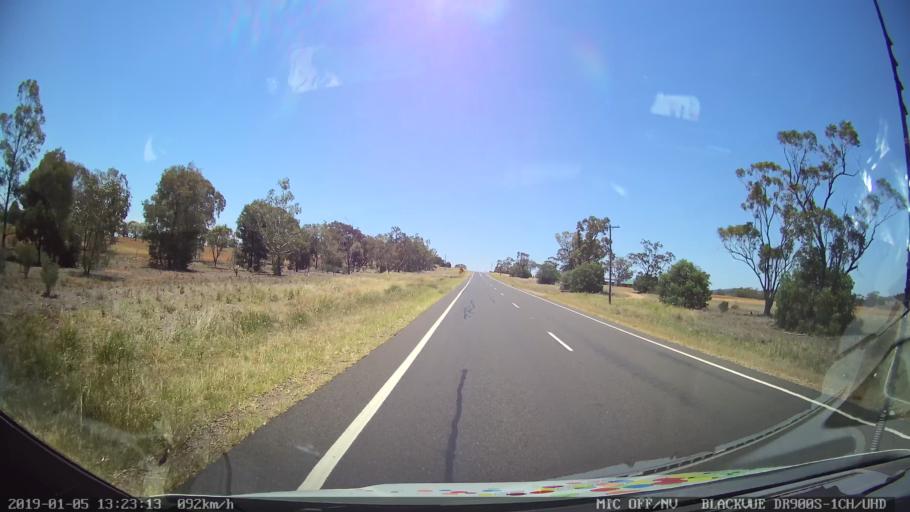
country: AU
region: New South Wales
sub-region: Gunnedah
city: Gunnedah
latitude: -31.0798
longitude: 149.9723
